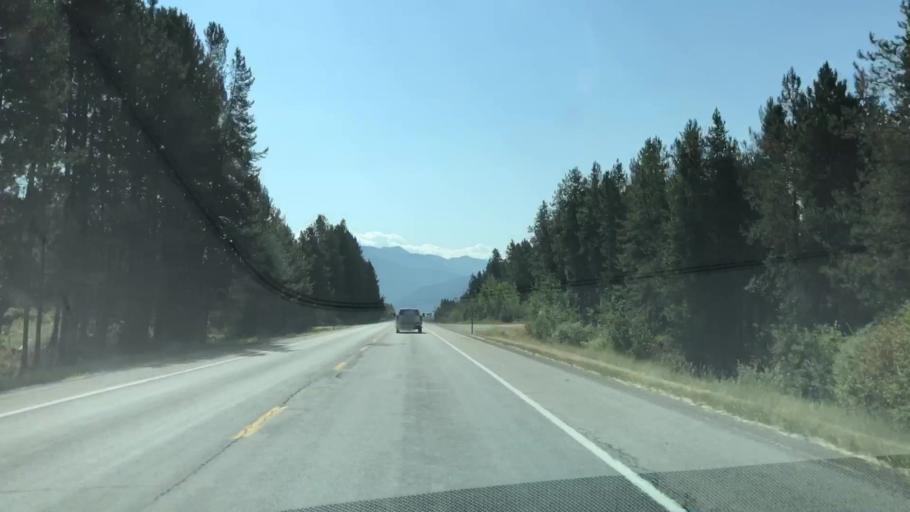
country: US
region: Wyoming
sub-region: Teton County
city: Hoback
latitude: 43.1980
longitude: -111.0417
